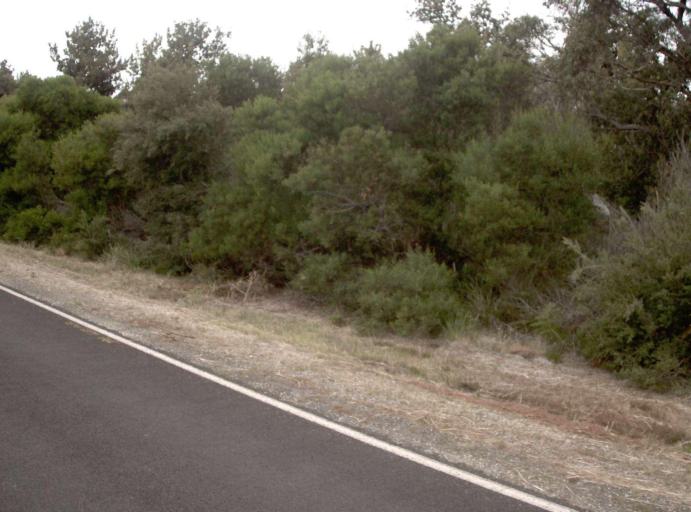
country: AU
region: Victoria
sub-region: East Gippsland
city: Bairnsdale
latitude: -38.0812
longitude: 147.5326
